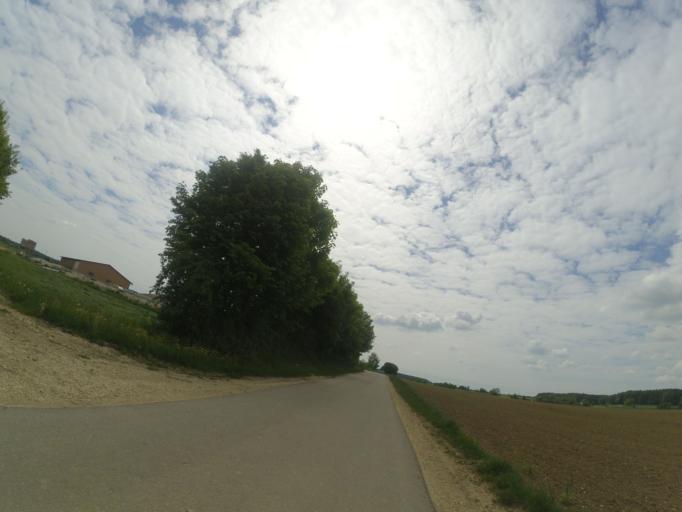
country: DE
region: Baden-Wuerttemberg
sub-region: Tuebingen Region
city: Berghulen
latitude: 48.4516
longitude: 9.7709
